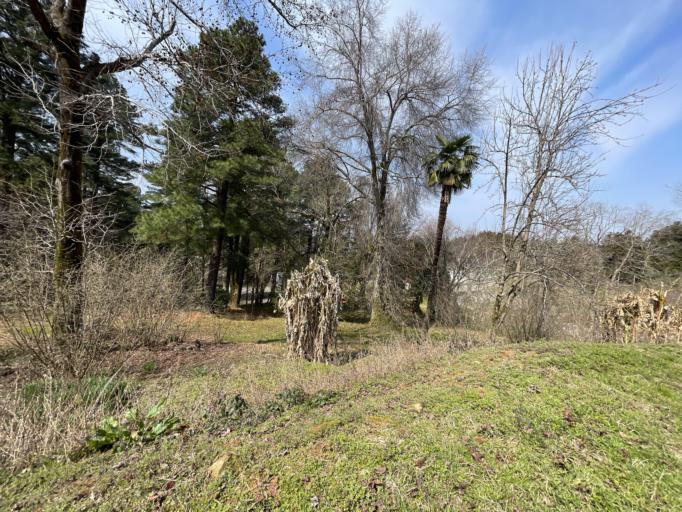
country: GE
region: Ajaria
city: Makhinjauri
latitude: 41.7046
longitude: 41.7217
